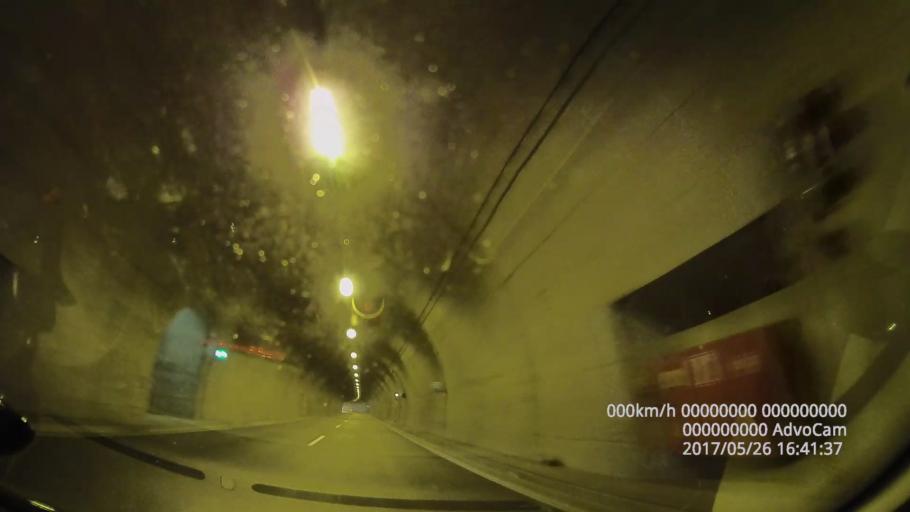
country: GR
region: Central Greece
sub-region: Nomos Fthiotidos
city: Stylida
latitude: 38.9035
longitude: 22.5441
